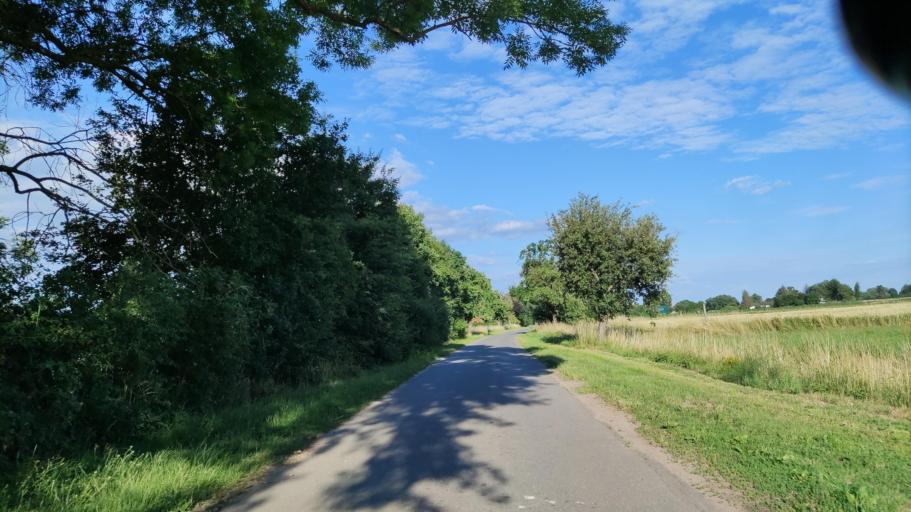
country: DE
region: Brandenburg
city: Lanz
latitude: 53.0403
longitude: 11.5487
